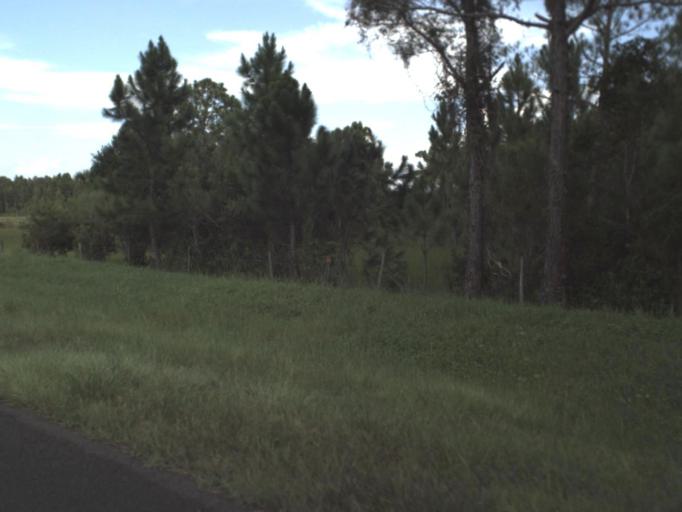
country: US
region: Florida
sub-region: Pasco County
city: Wesley Chapel
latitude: 28.2125
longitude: -82.3533
